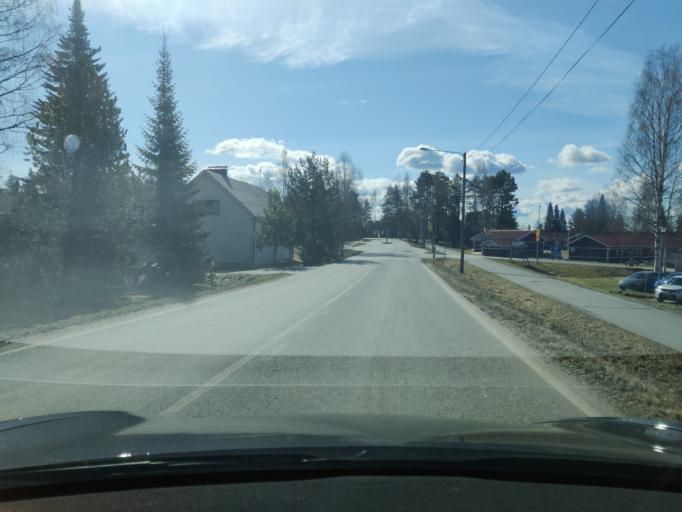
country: FI
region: Northern Savo
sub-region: Kuopio
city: Vehmersalmi
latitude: 62.7652
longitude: 28.0209
